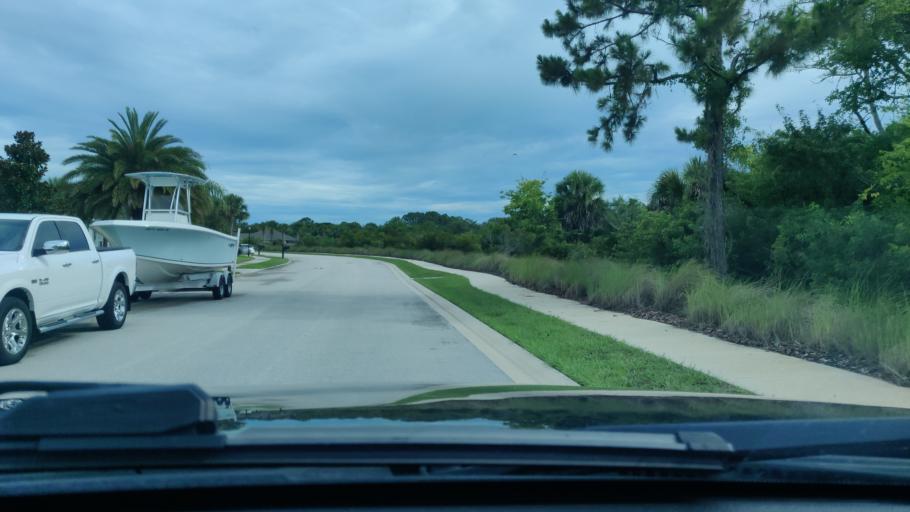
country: US
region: Florida
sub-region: Flagler County
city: Flagler Beach
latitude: 29.5154
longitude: -81.1587
